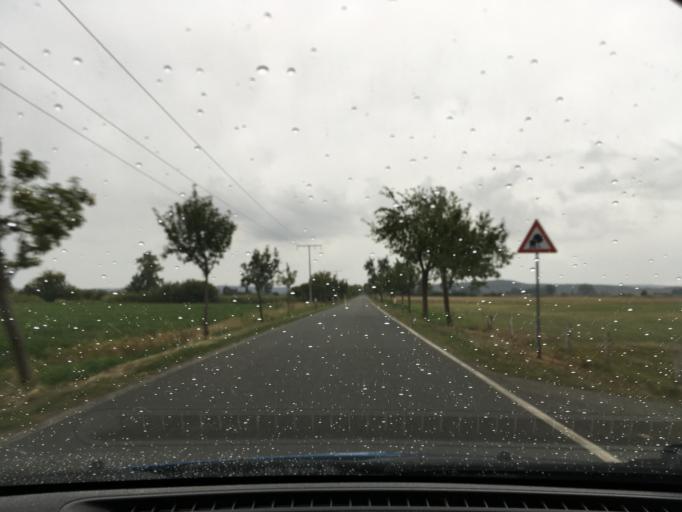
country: DE
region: Lower Saxony
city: Hitzacker
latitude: 53.2245
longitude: 10.9885
